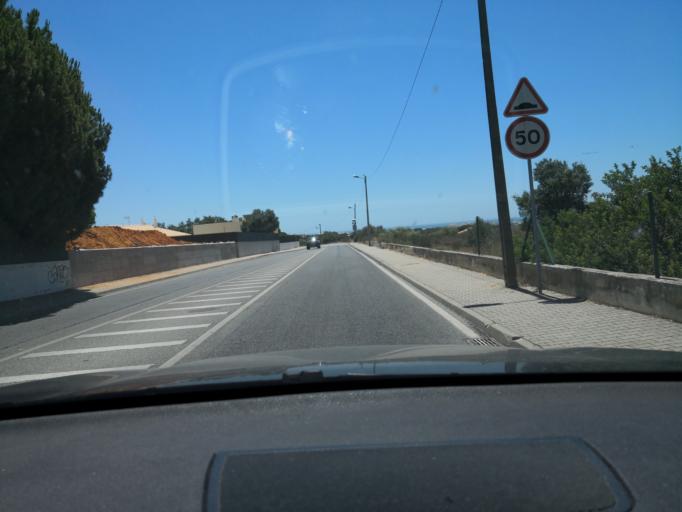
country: PT
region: Faro
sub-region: Albufeira
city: Ferreiras
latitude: 37.1071
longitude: -8.2003
